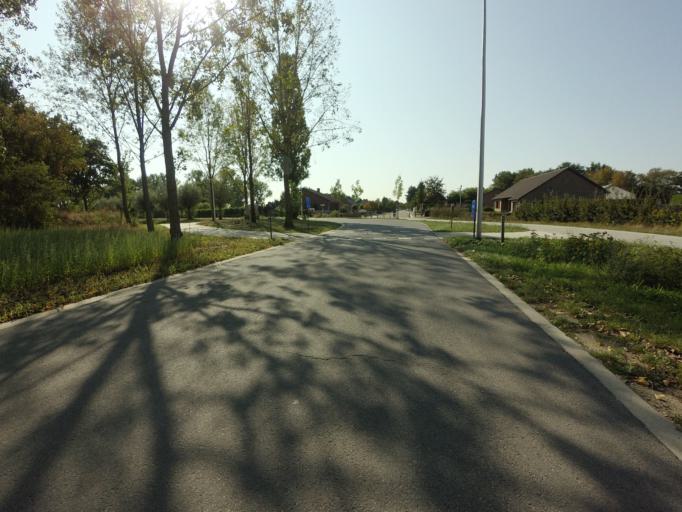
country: BE
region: Flanders
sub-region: Provincie Limburg
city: Maaseik
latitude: 51.1362
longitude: 5.8169
